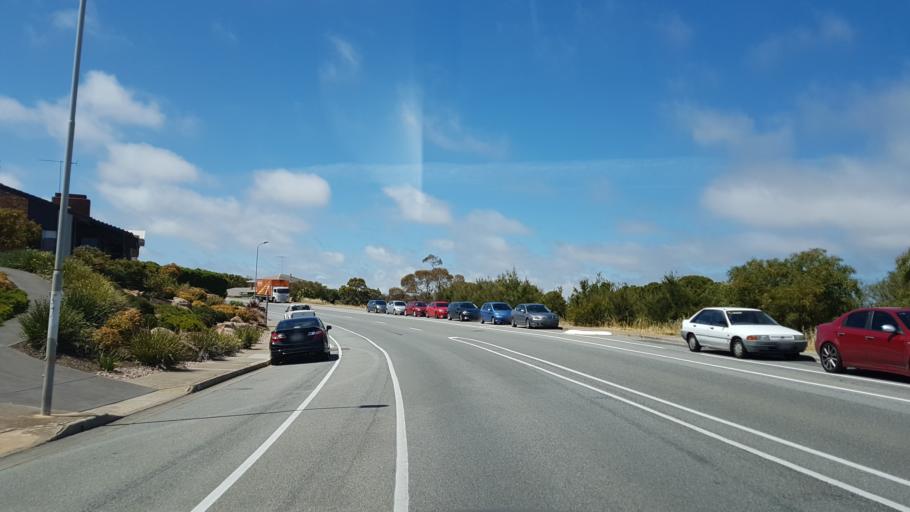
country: AU
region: South Australia
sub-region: Marion
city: Marino
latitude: -35.0683
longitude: 138.5065
